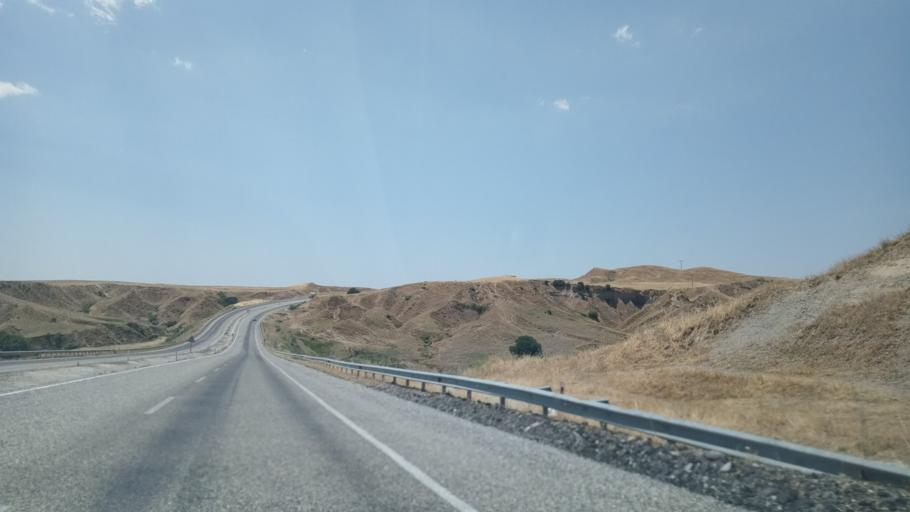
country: TR
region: Batman
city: Bekirhan
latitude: 38.1405
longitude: 41.2771
